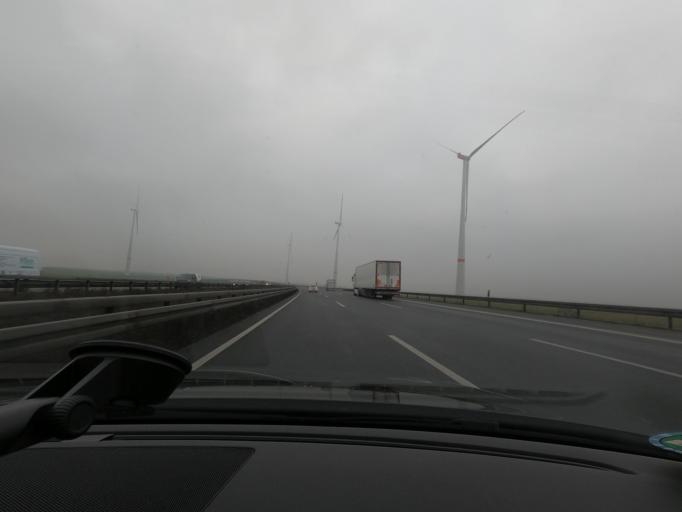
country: DE
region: North Rhine-Westphalia
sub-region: Regierungsbezirk Dusseldorf
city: Juchen
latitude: 51.0498
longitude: 6.5006
